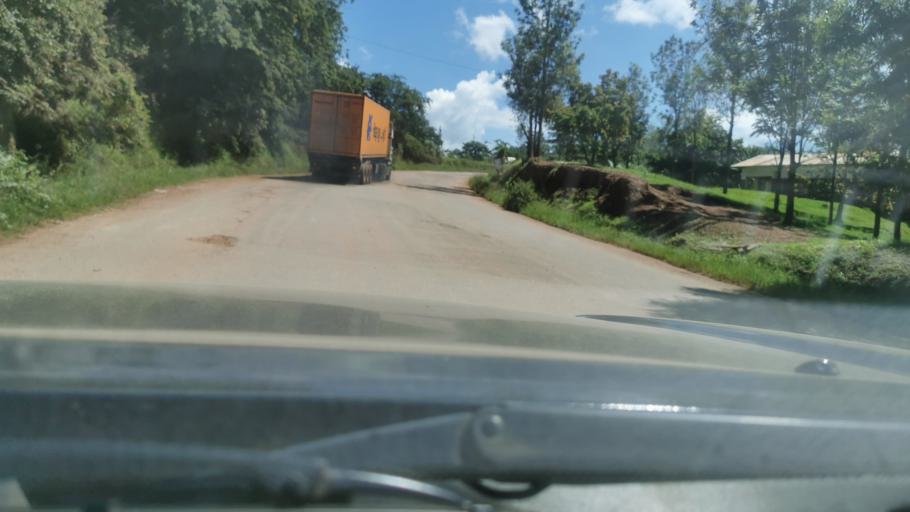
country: TZ
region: Kagera
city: Ngara
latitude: -2.3841
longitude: 30.7874
